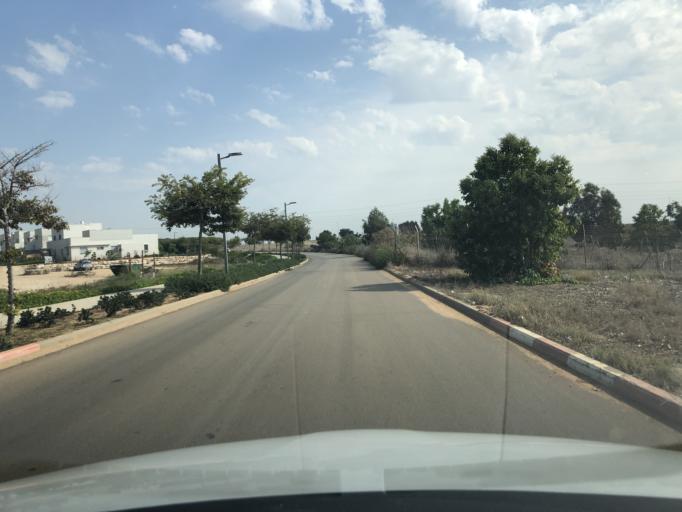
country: IL
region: Tel Aviv
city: Kefar Shemaryahu
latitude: 32.2130
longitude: 34.8236
